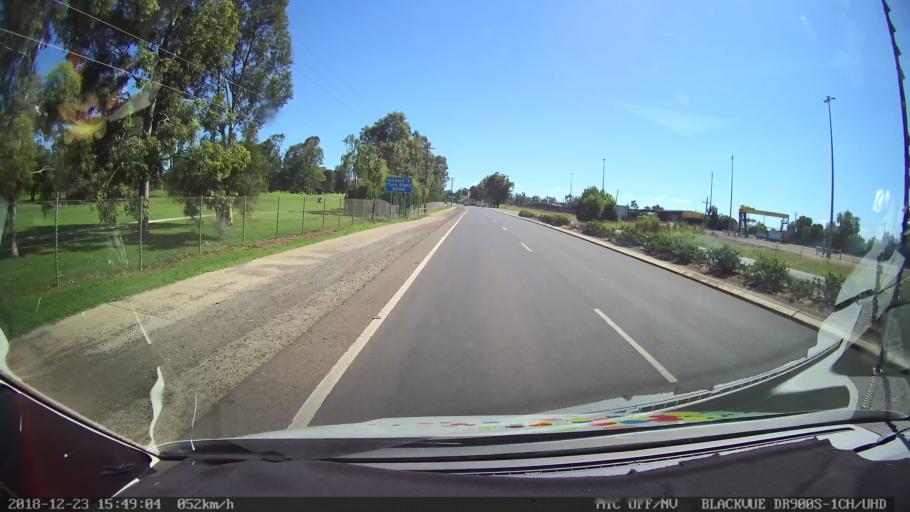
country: AU
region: New South Wales
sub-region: Tamworth Municipality
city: South Tamworth
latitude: -31.0967
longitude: 150.9093
